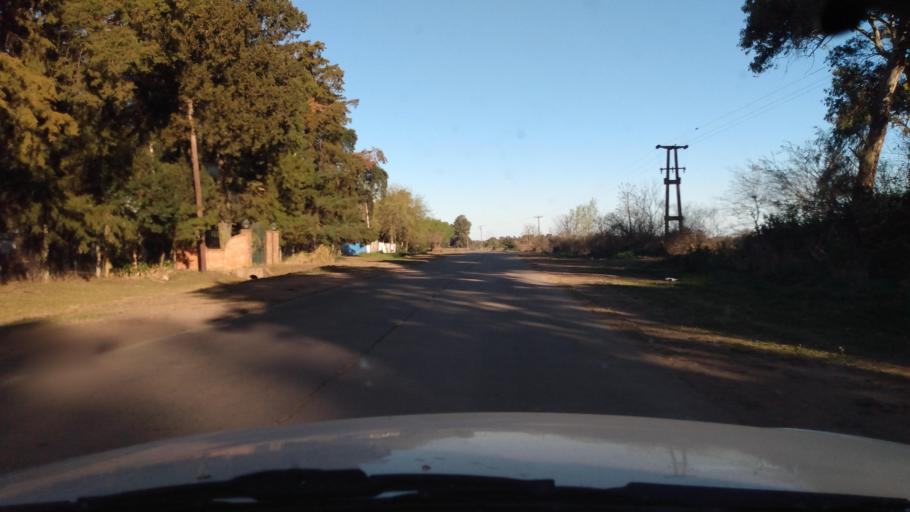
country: AR
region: Buenos Aires
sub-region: Partido de Mercedes
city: Mercedes
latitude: -34.6104
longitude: -59.2838
